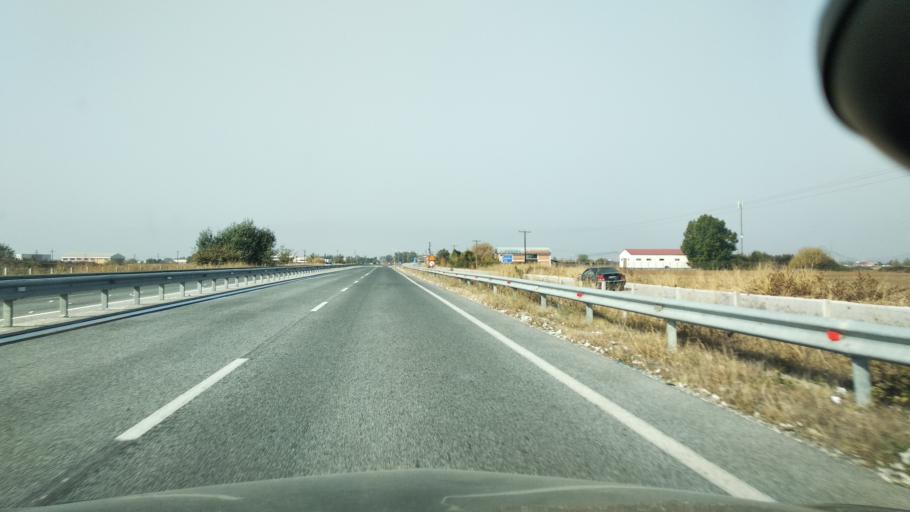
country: GR
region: Thessaly
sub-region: Trikala
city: Megalochori
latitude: 39.5622
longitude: 21.8660
